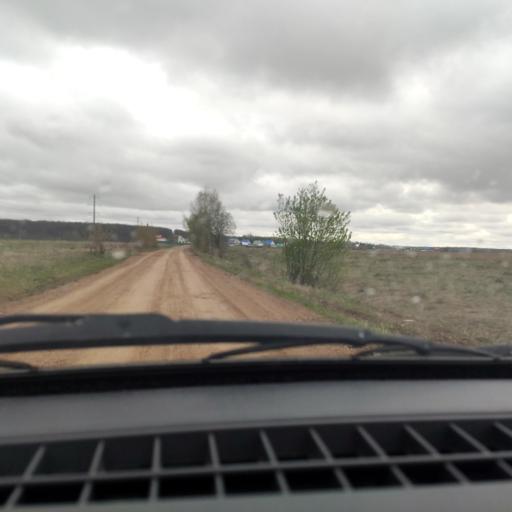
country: RU
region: Bashkortostan
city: Iglino
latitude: 54.7490
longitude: 56.2542
